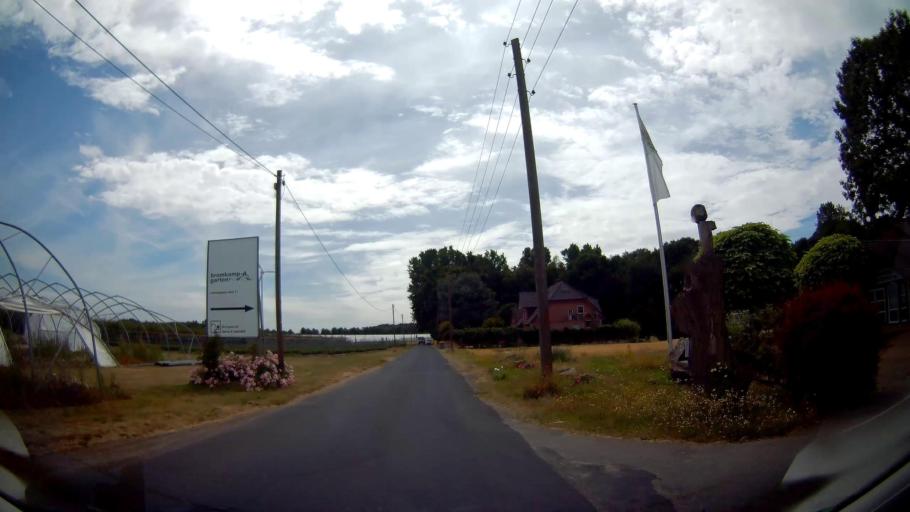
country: DE
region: North Rhine-Westphalia
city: Dorsten
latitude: 51.6162
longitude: 6.9450
